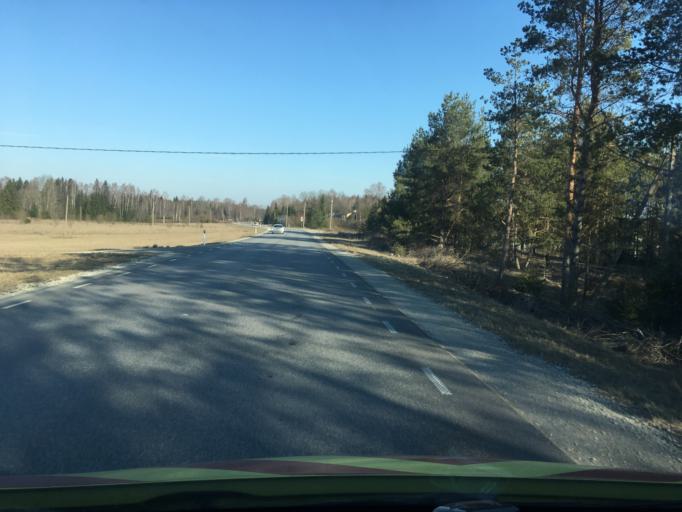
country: EE
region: Raplamaa
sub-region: Rapla vald
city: Rapla
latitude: 59.0072
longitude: 24.8419
